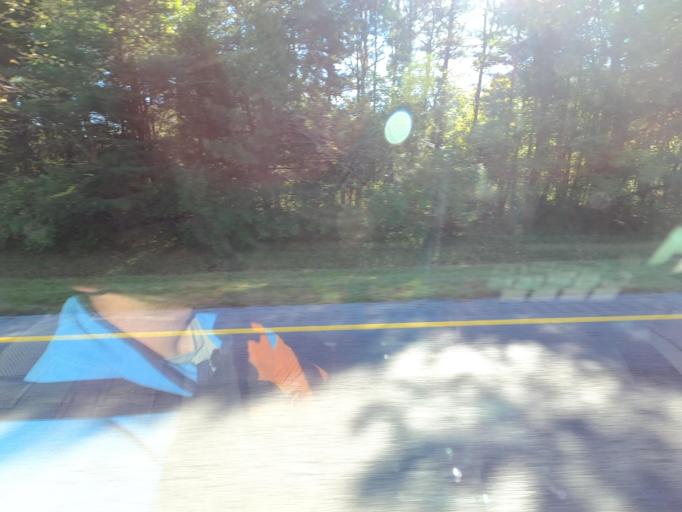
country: US
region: Tennessee
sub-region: Cheatham County
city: Kingston Springs
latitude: 36.0551
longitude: -87.1397
